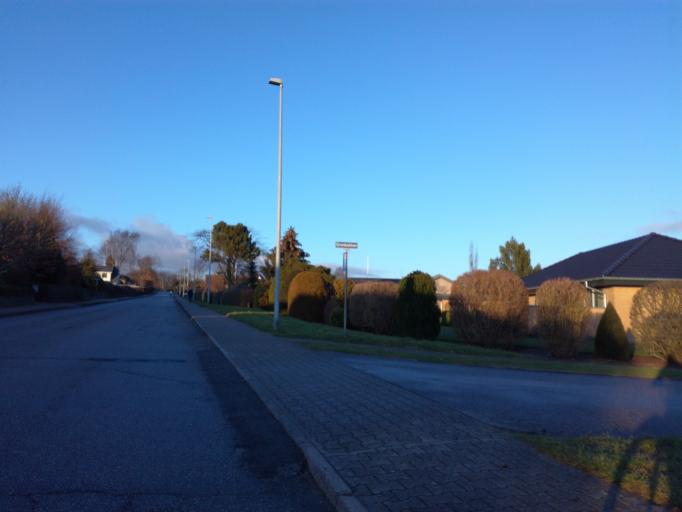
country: DK
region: South Denmark
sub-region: Fredericia Kommune
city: Taulov
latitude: 55.5357
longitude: 9.6101
